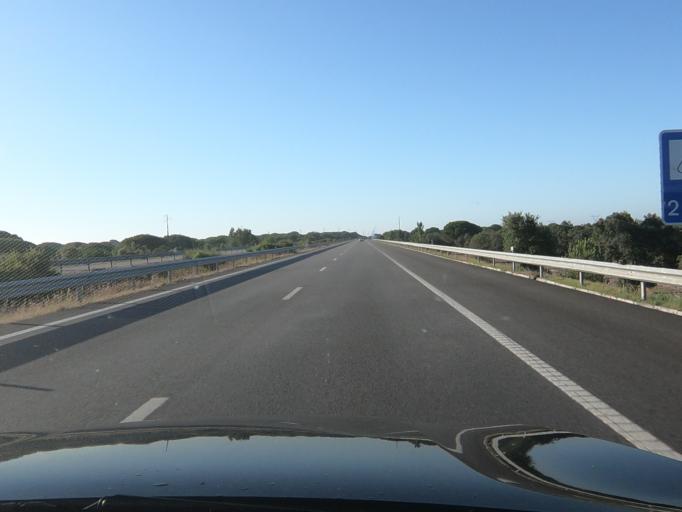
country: PT
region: Setubal
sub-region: Alcacer do Sal
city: Alcacer do Sal
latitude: 38.5344
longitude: -8.6016
